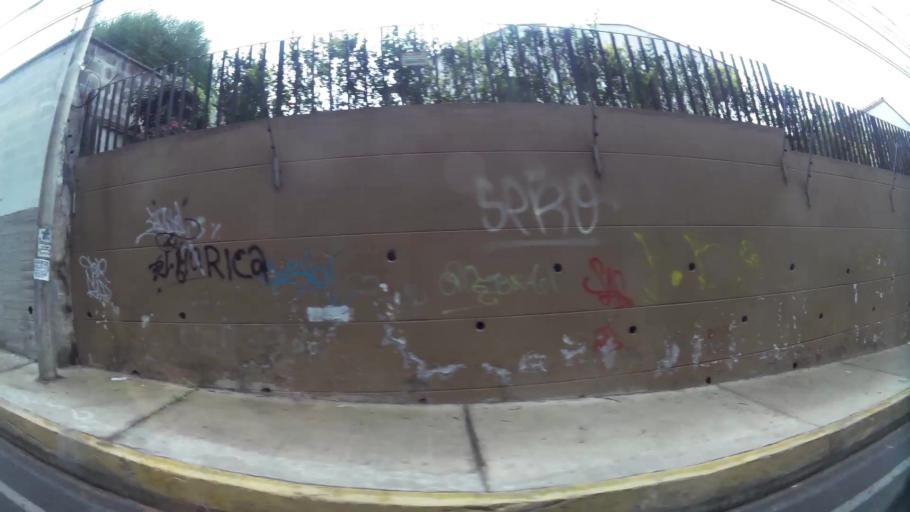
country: EC
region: Pichincha
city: Quito
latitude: -0.2672
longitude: -78.4713
